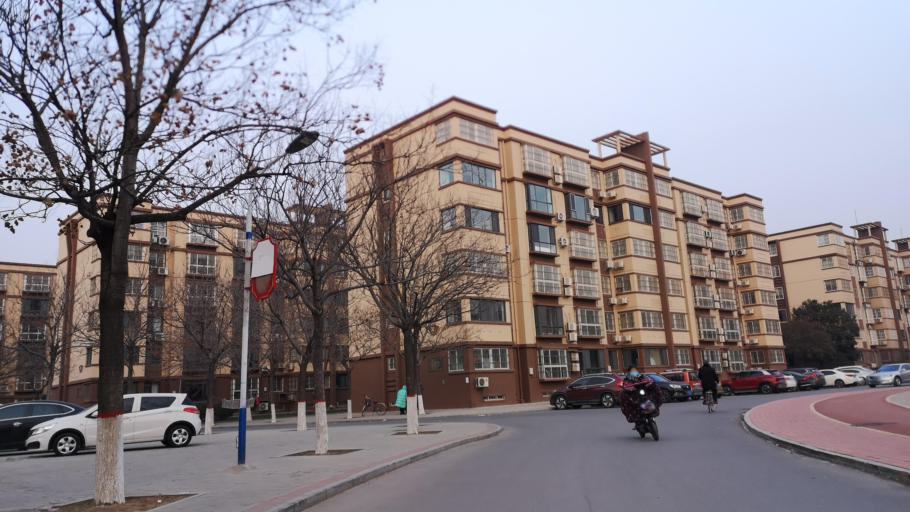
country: CN
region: Henan Sheng
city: Zhongyuanlu
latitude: 35.7878
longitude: 115.0783
